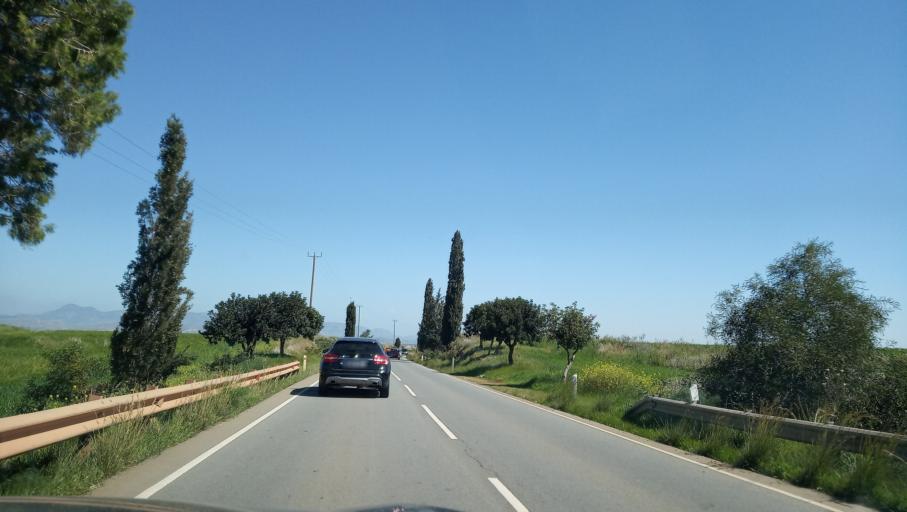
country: CY
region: Lefkosia
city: Astromeritis
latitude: 35.1118
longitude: 32.9885
